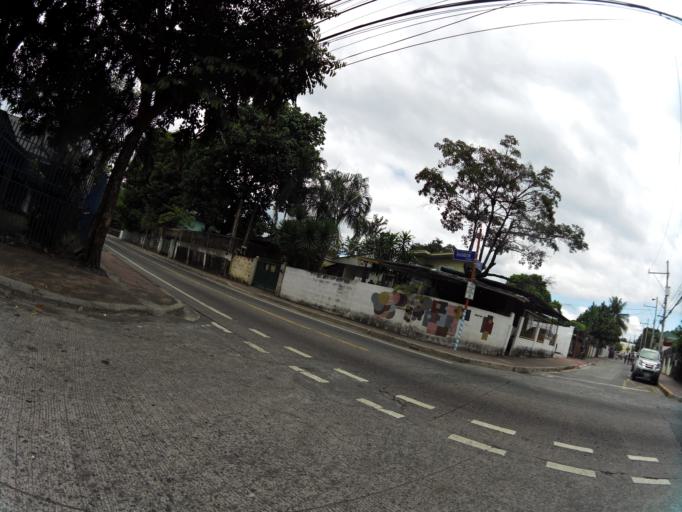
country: PH
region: Calabarzon
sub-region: Province of Rizal
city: Antipolo
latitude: 14.6406
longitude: 121.1163
